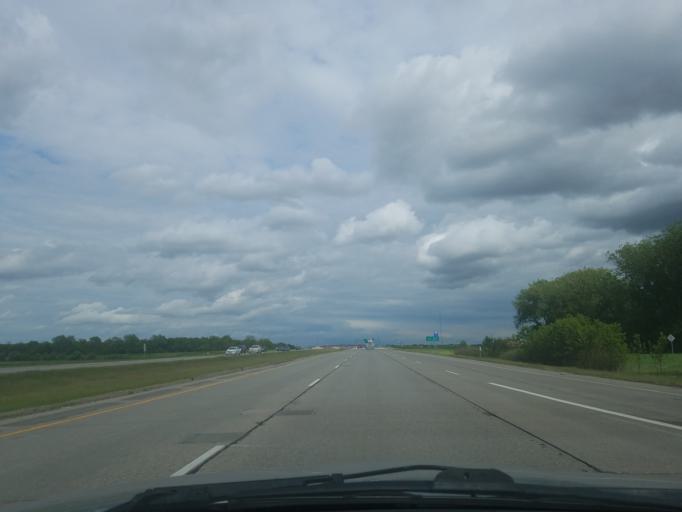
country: US
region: North Dakota
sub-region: Cass County
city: West Fargo
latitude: 46.8773
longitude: -96.9639
